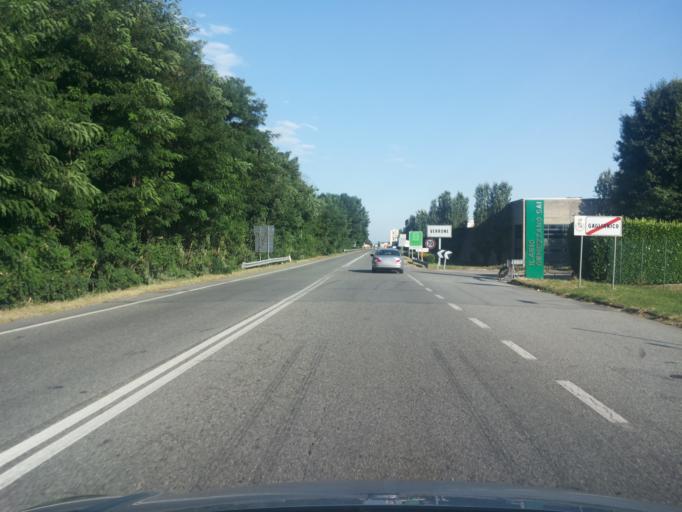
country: IT
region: Piedmont
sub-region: Provincia di Biella
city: Verrone
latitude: 45.5192
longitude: 8.1012
